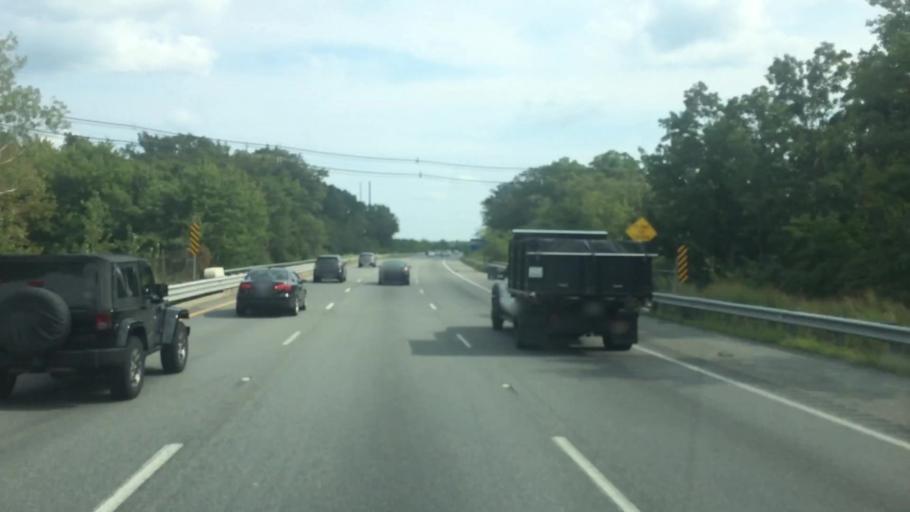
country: US
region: Massachusetts
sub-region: Worcester County
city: Milford
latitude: 42.1551
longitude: -71.4886
